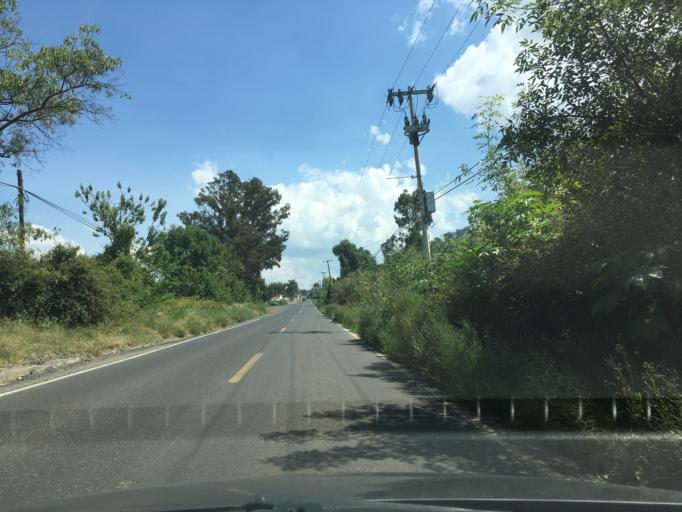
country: MX
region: Michoacan
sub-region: Morelia
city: La Mintzita (Piedra Dura)
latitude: 19.6398
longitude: -101.2694
